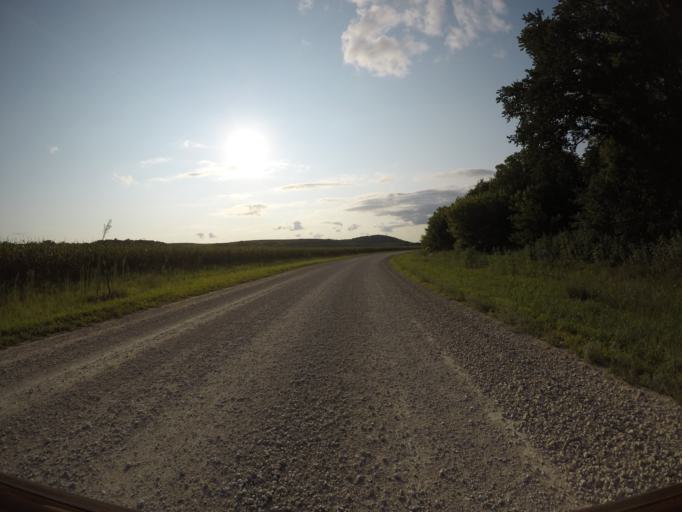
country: US
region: Kansas
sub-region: Wabaunsee County
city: Alma
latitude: 38.9520
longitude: -96.2469
